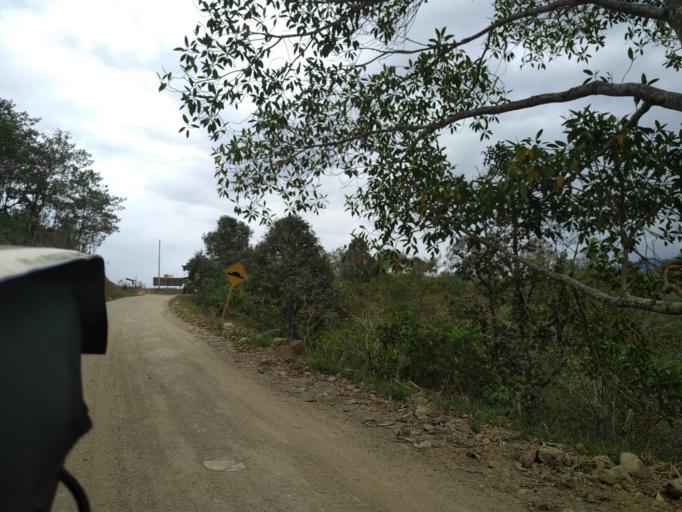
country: PE
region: Cajamarca
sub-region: Provincia de San Ignacio
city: Namballe
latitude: -4.9361
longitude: -79.1053
